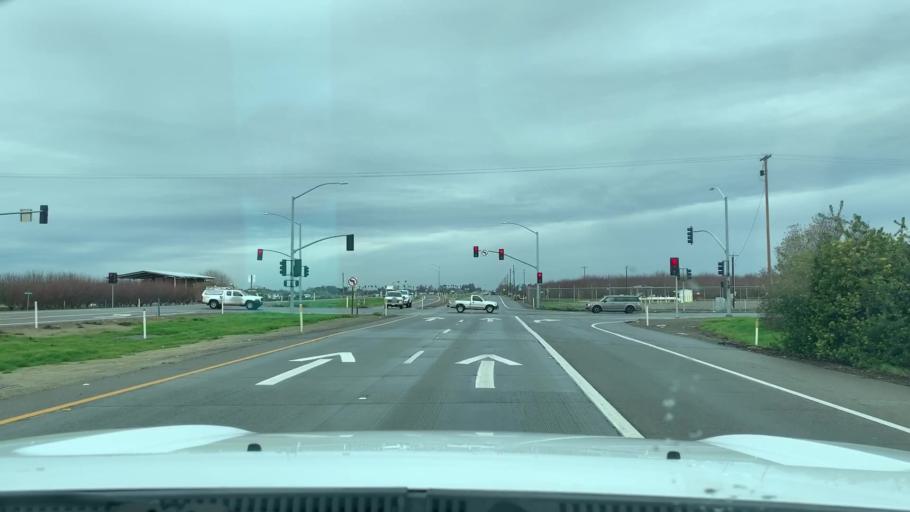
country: US
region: California
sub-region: Kings County
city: Lemoore
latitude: 36.3129
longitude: -119.8077
